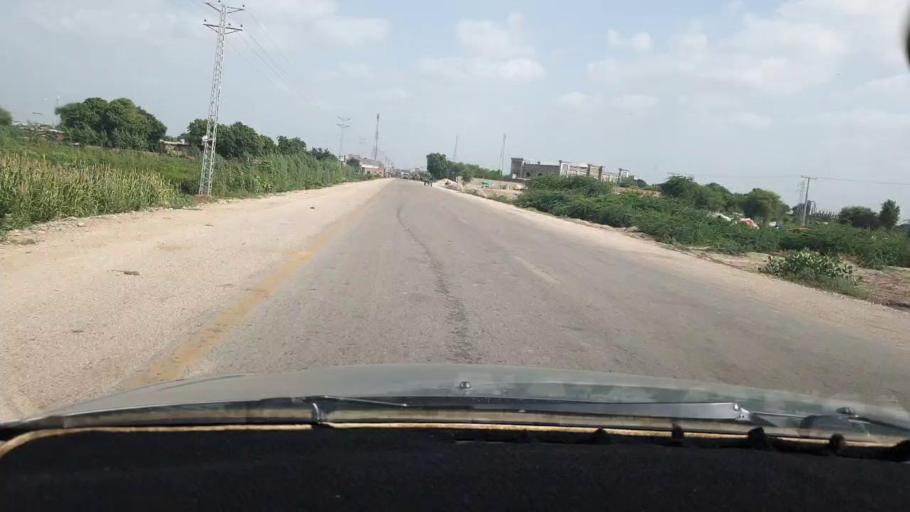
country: PK
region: Sindh
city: Naukot
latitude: 24.8599
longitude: 69.3938
